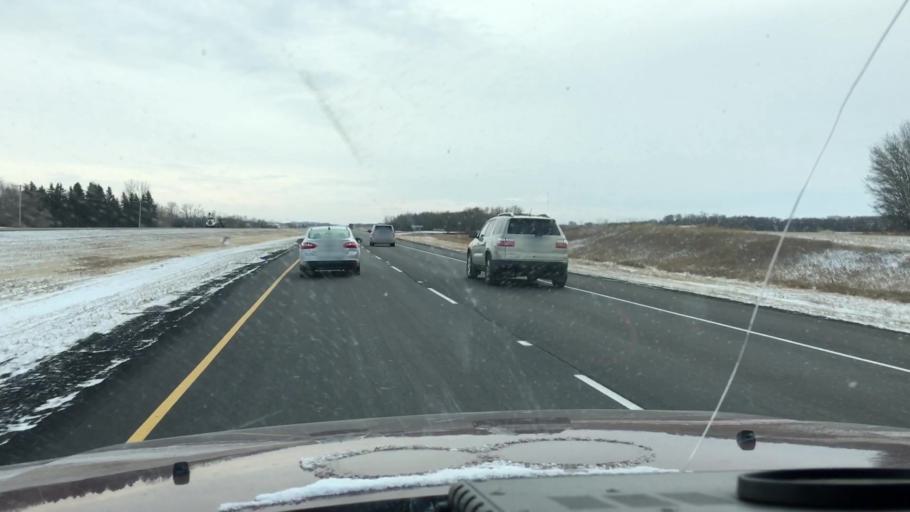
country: CA
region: Saskatchewan
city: Saskatoon
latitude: 52.0160
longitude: -106.5755
